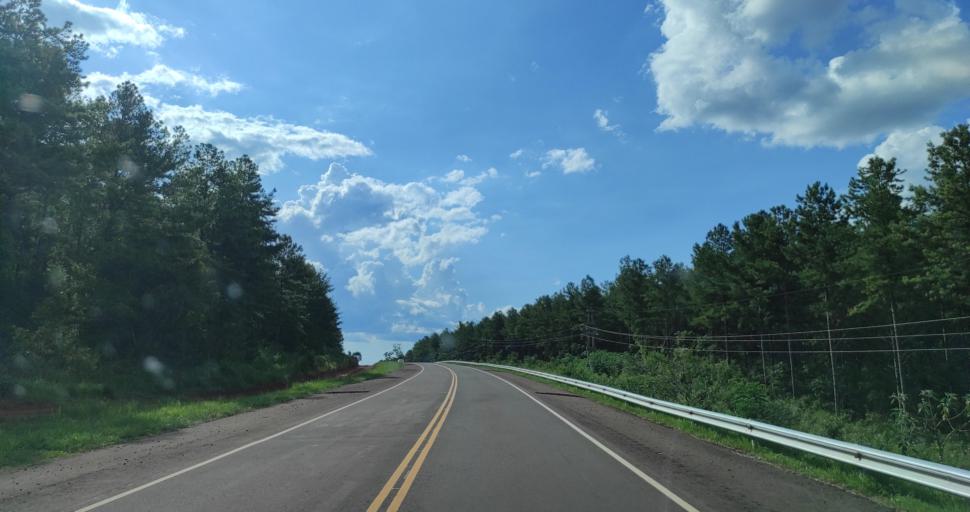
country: AR
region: Misiones
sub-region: Departamento de San Pedro
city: San Pedro
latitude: -26.3533
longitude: -53.9602
